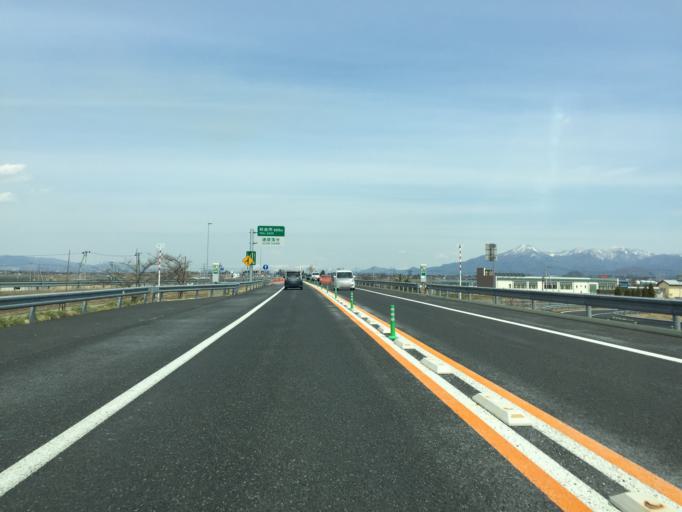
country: JP
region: Yamagata
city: Tendo
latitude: 38.3637
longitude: 140.3460
